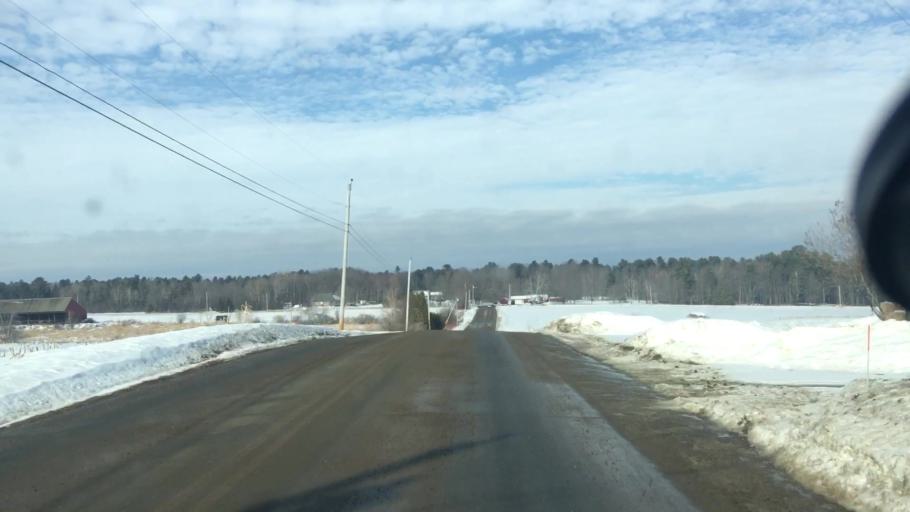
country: US
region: Maine
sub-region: Penobscot County
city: Levant
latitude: 44.8583
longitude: -68.8786
